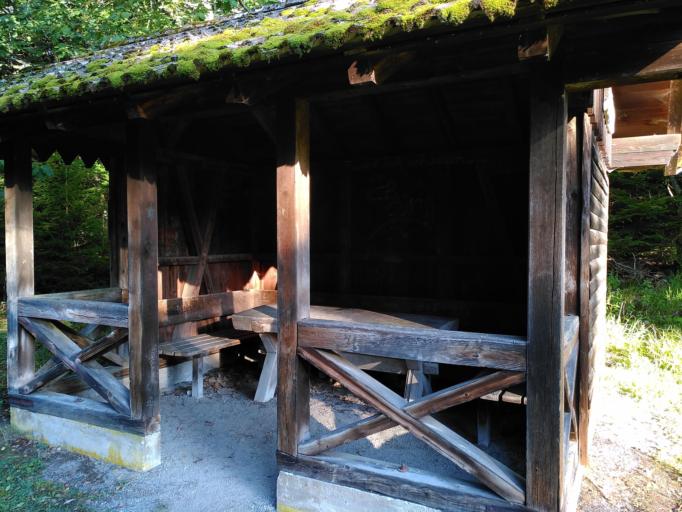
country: DE
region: Baden-Wuerttemberg
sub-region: Karlsruhe Region
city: Bad Wildbad
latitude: 48.7749
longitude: 8.5496
